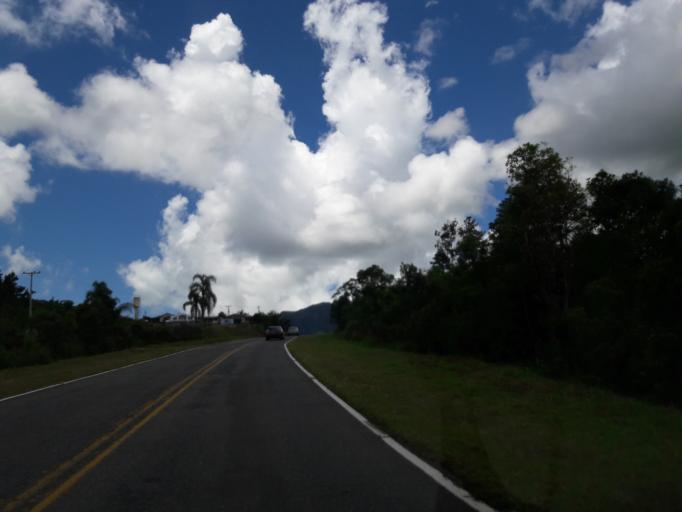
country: BR
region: Parana
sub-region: Campina Grande Do Sul
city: Campina Grande do Sul
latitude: -25.3124
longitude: -48.9321
